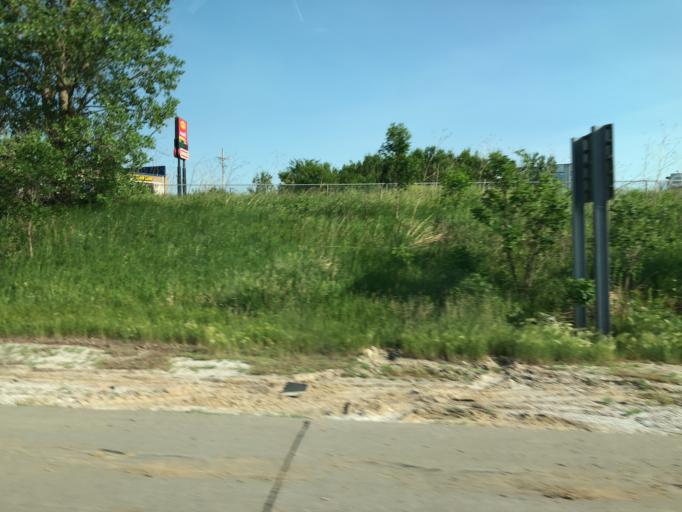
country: US
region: Nebraska
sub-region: Sarpy County
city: Gretna
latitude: 41.0930
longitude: -96.2561
